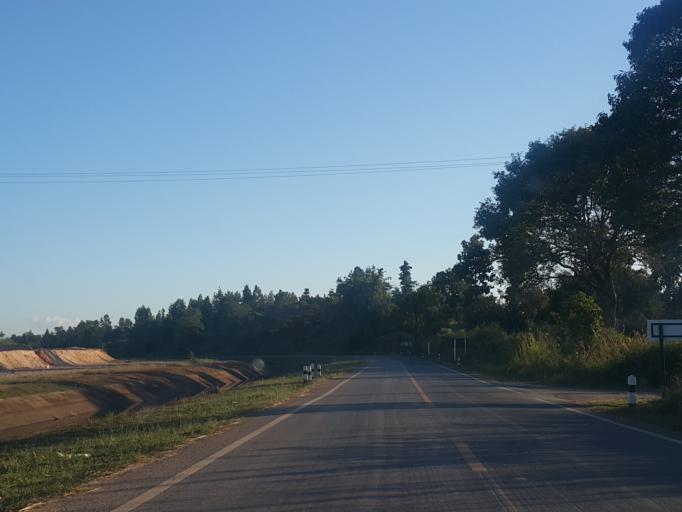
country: TH
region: Chiang Mai
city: San Sai
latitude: 18.8991
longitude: 99.1486
